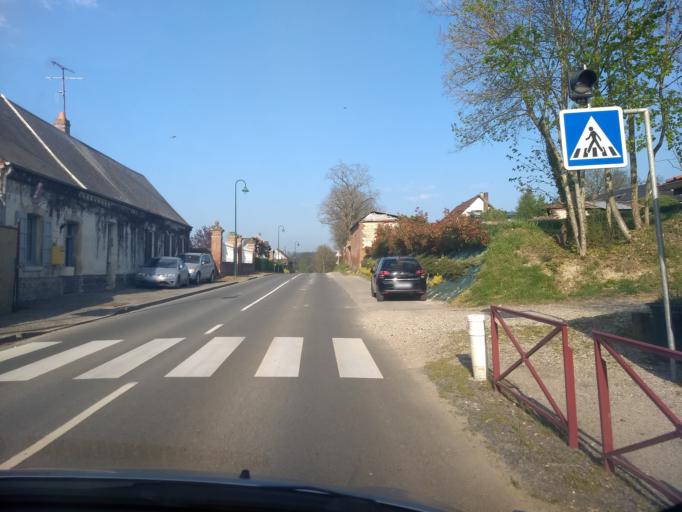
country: FR
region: Picardie
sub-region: Departement de la Somme
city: Corbie
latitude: 50.0080
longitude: 2.4890
